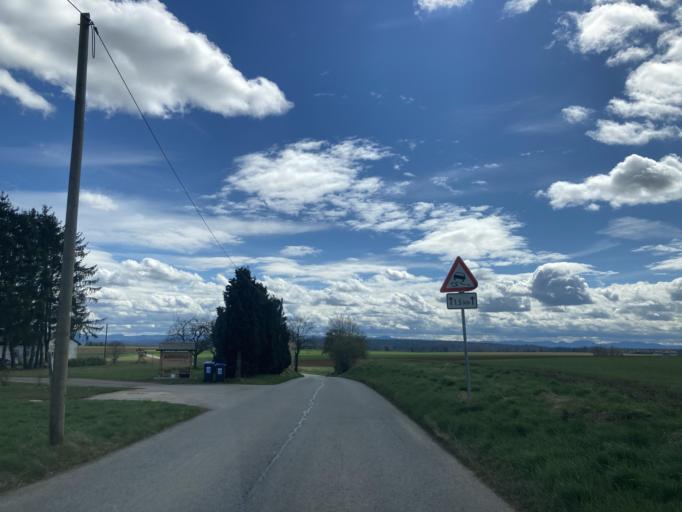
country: DE
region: Baden-Wuerttemberg
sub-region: Regierungsbezirk Stuttgart
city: Bondorf
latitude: 48.4671
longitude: 8.8245
